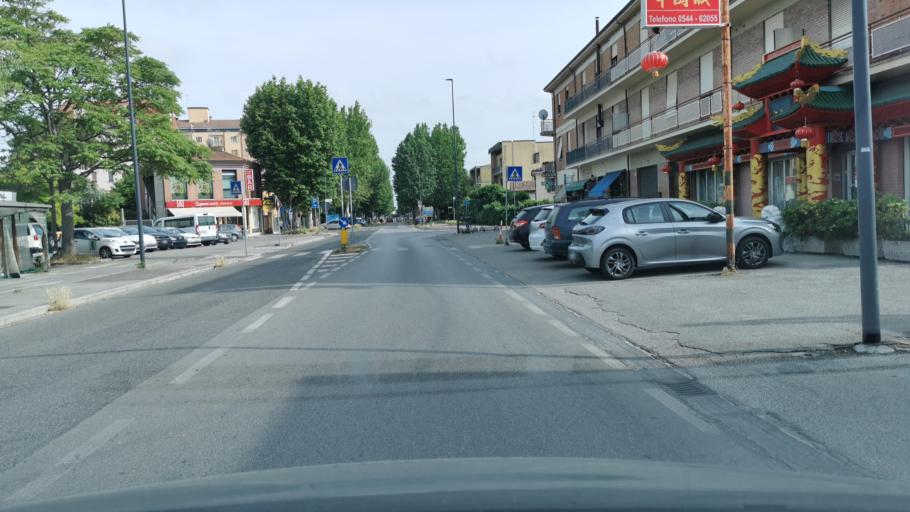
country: IT
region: Emilia-Romagna
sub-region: Provincia di Ravenna
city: Ravenna
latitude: 44.4088
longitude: 12.2079
